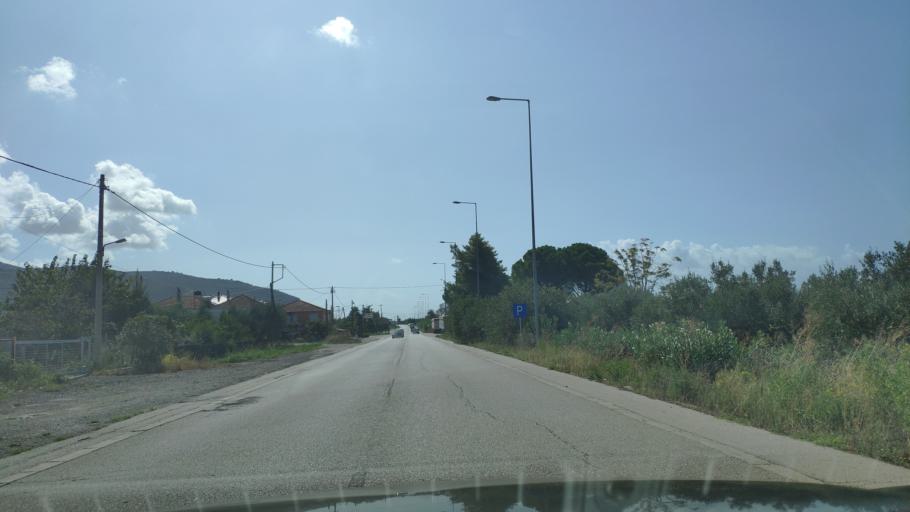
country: GR
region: West Greece
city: Aitoliko
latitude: 38.4782
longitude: 21.3542
